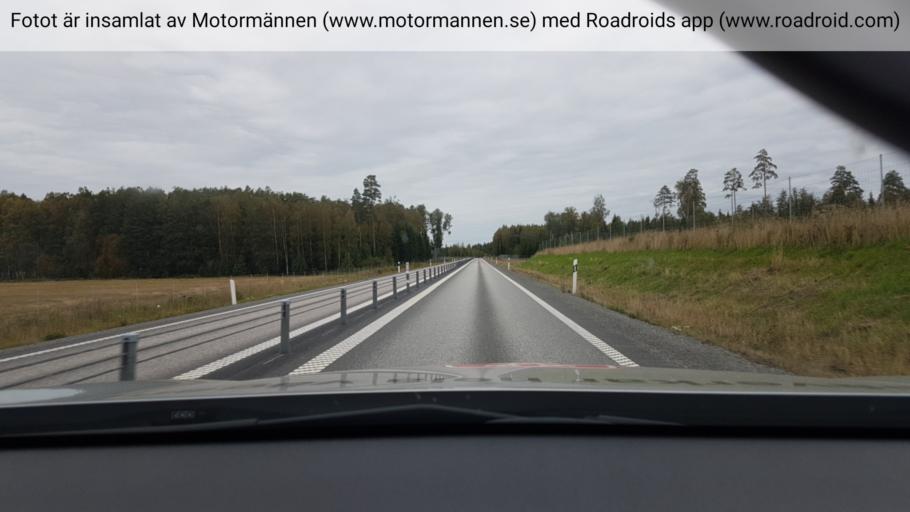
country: SE
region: Uppsala
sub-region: Heby Kommun
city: Heby
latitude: 60.0342
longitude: 16.8704
